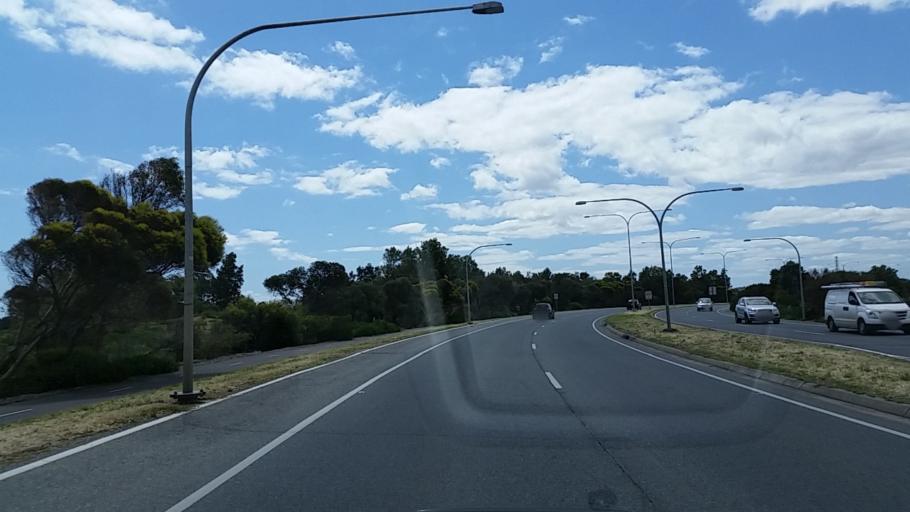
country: AU
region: South Australia
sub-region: Adelaide
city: Glenelg
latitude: -34.9578
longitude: 138.5140
